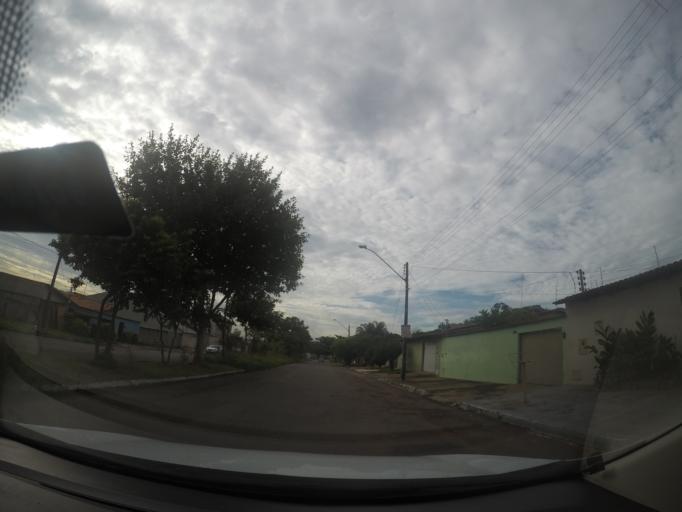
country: BR
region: Goias
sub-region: Goiania
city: Goiania
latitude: -16.6843
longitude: -49.2013
